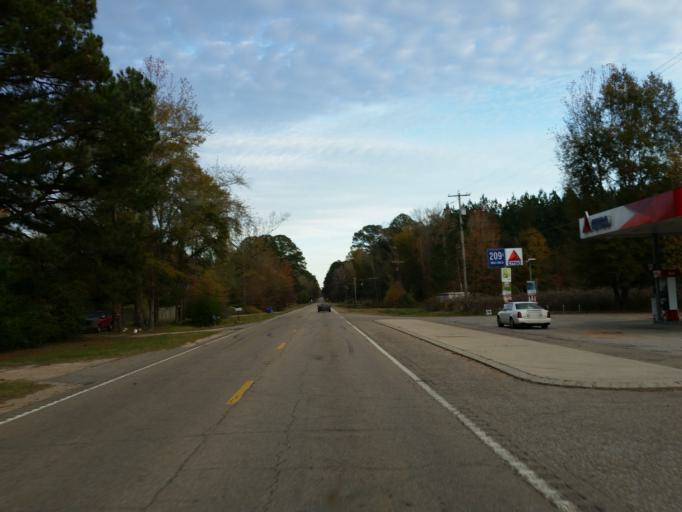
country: US
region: Mississippi
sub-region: Lauderdale County
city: Marion
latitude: 32.4193
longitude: -88.5243
